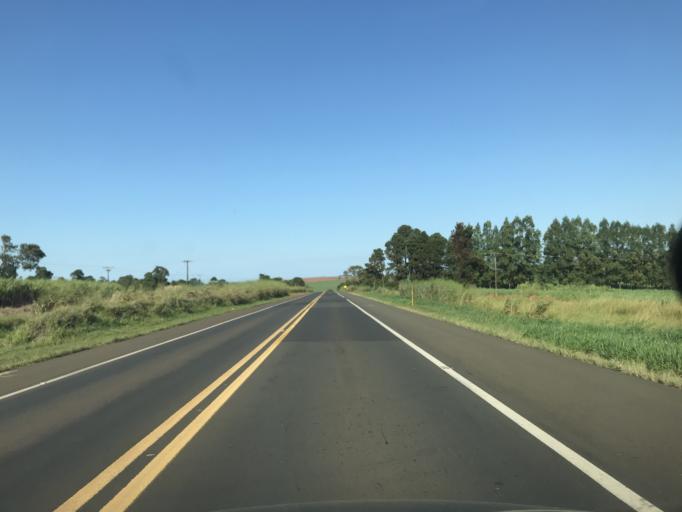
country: BR
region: Parana
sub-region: Centenario Do Sul
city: Centenario do Sul
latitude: -22.5764
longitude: -51.7054
